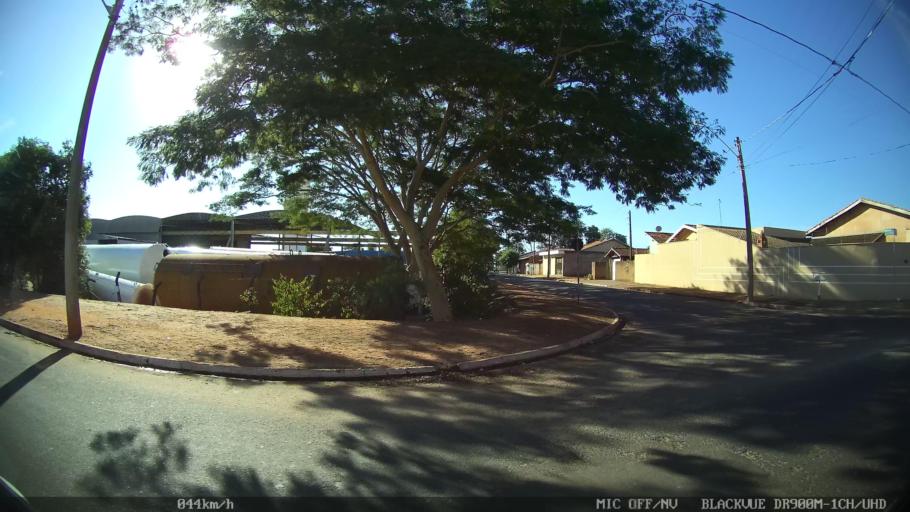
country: BR
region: Sao Paulo
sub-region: Olimpia
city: Olimpia
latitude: -20.7267
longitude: -48.9032
